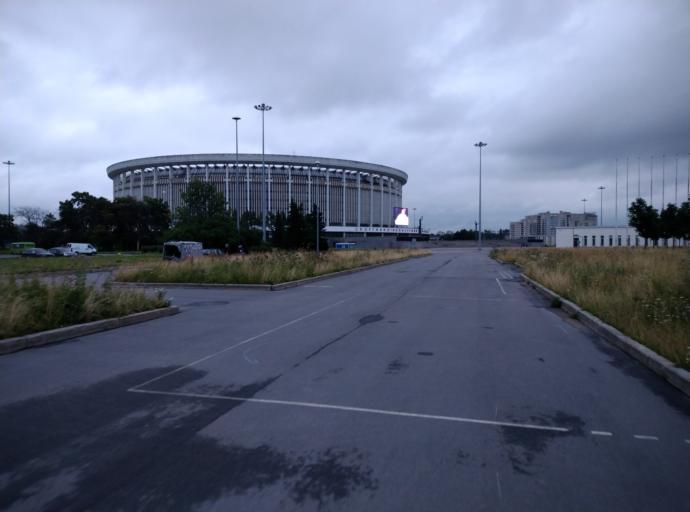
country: RU
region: St.-Petersburg
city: Kupchino
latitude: 59.8711
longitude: 30.3377
